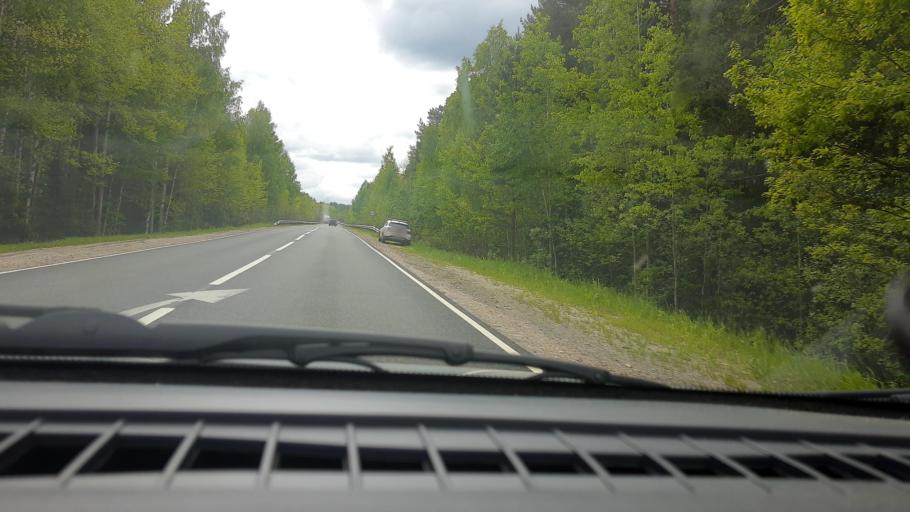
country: RU
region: Nizjnij Novgorod
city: Krasnyye Baki
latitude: 57.1249
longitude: 45.2113
